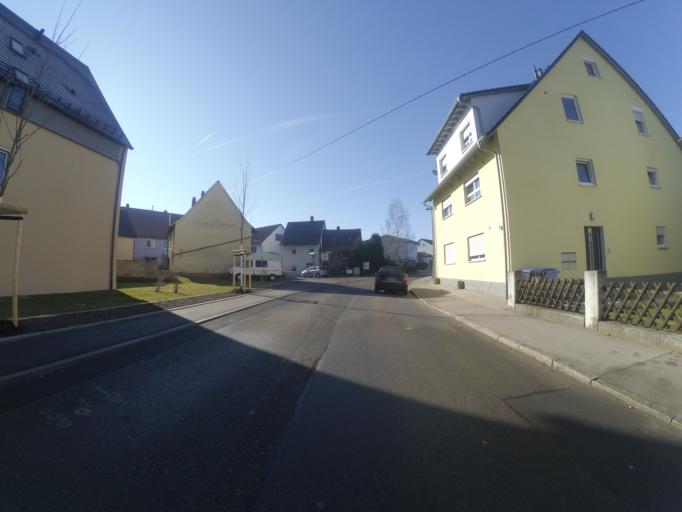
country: DE
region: Baden-Wuerttemberg
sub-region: Tuebingen Region
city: Erbach
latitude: 48.3299
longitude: 9.9325
